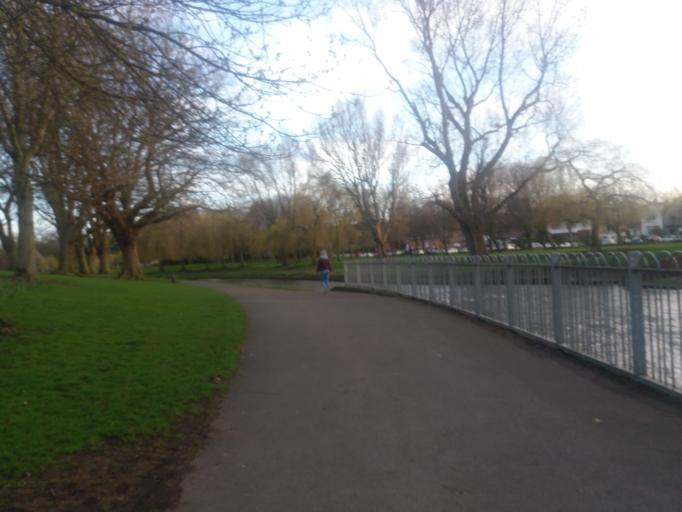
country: IE
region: Leinster
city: Glasnevin
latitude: 53.3709
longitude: -6.2626
